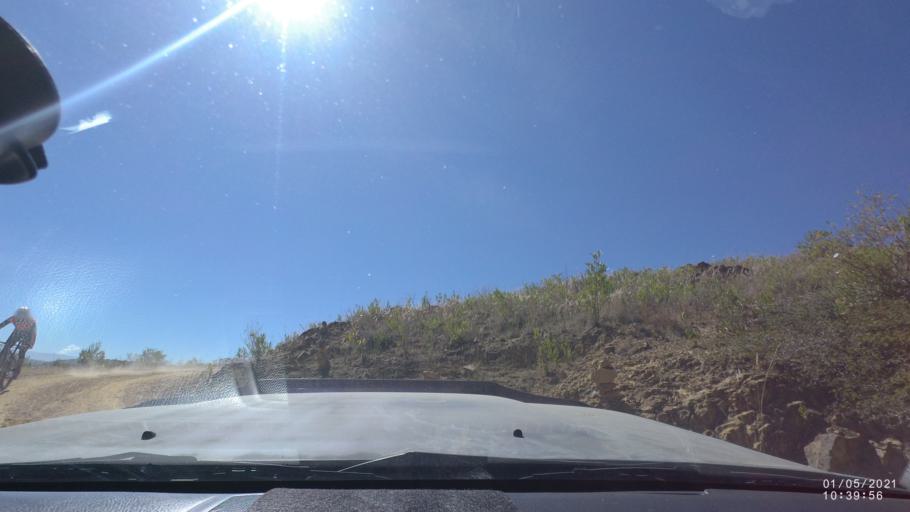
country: BO
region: Cochabamba
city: Capinota
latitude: -17.6062
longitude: -66.1836
